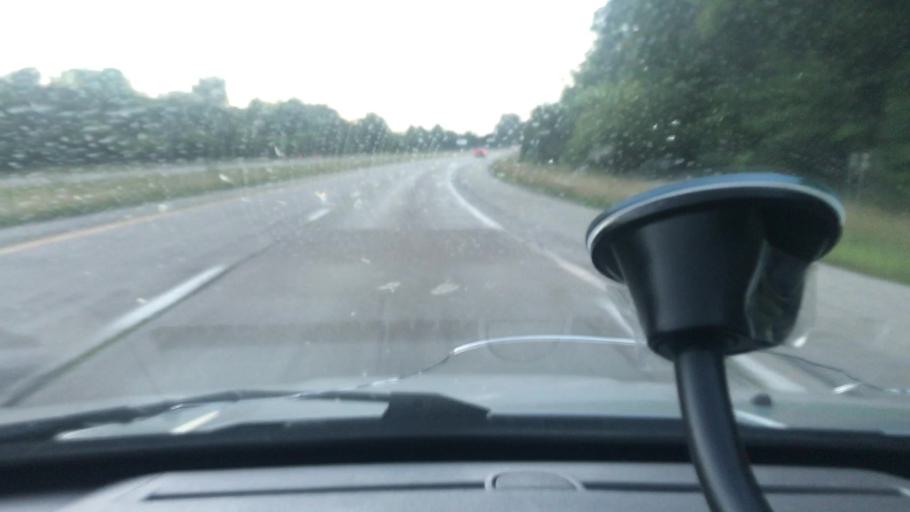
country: US
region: Illinois
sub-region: Peoria County
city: Bellevue
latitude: 40.7491
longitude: -89.6697
